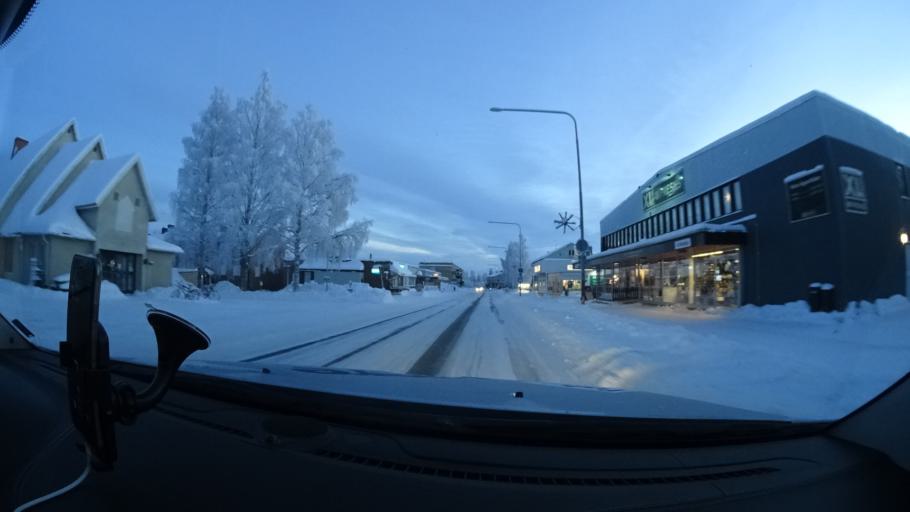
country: SE
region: Vaesterbotten
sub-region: Norsjo Kommun
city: Norsjoe
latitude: 64.9140
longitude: 19.4783
